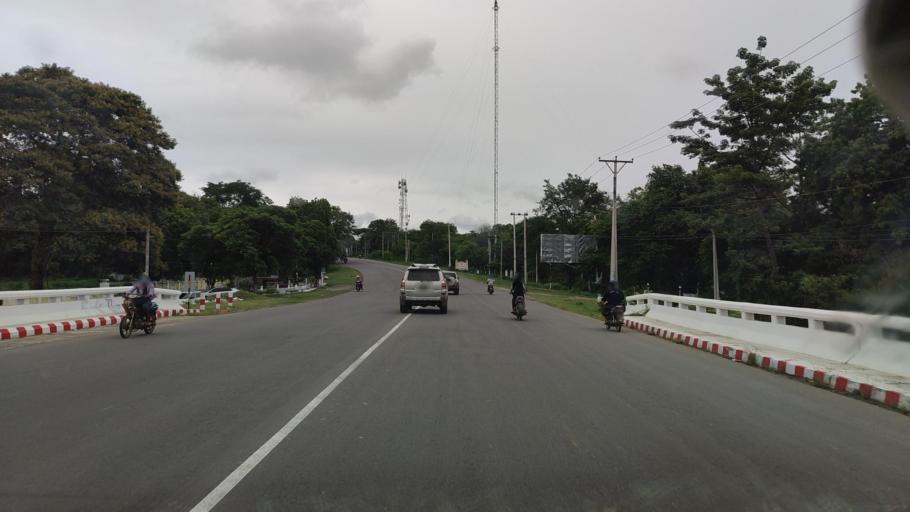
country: MM
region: Mandalay
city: Meiktila
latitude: 20.8664
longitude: 95.8683
